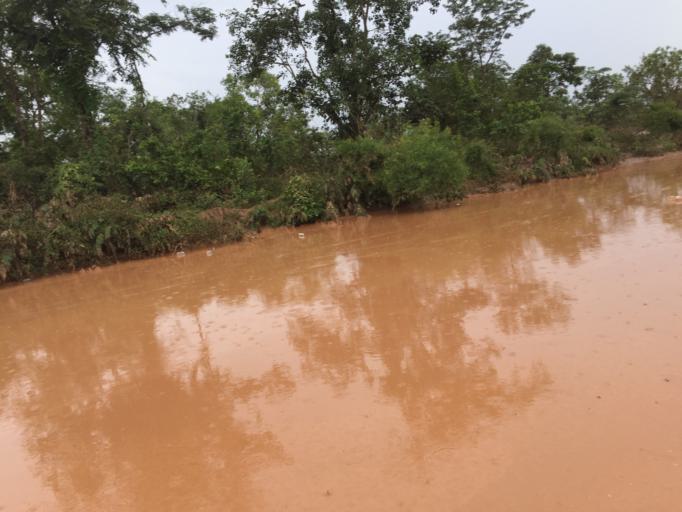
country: LA
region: Attapu
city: Attapu
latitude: 14.7042
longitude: 106.5210
